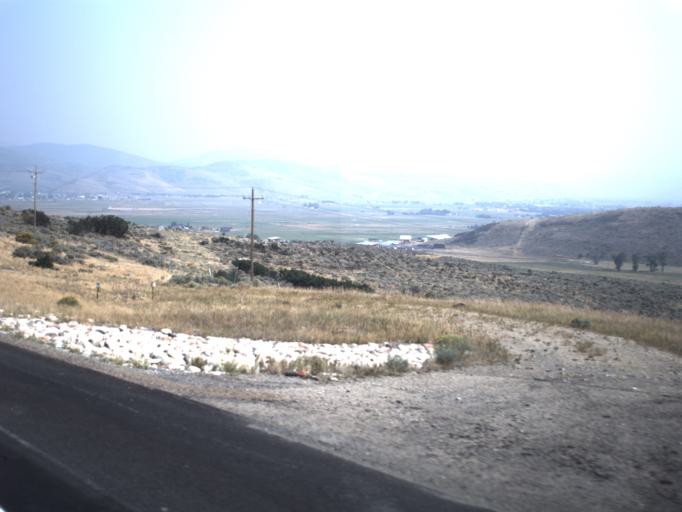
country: US
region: Utah
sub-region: Summit County
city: Kamas
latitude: 40.6373
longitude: -111.3339
